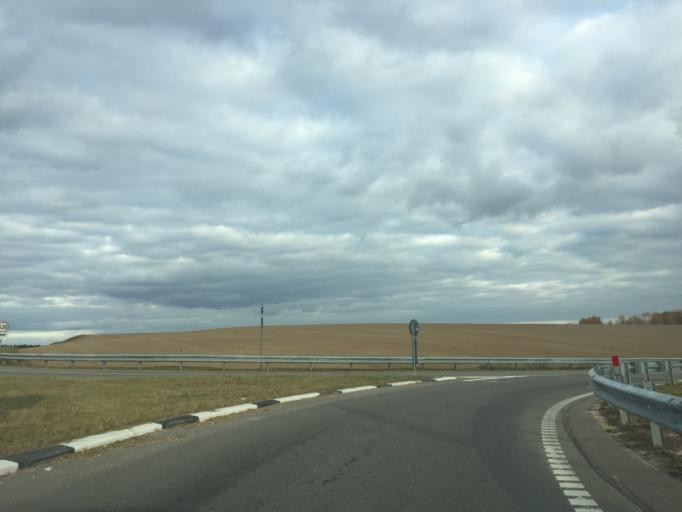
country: BY
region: Minsk
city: Pyatryshki
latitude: 54.0201
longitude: 27.1428
